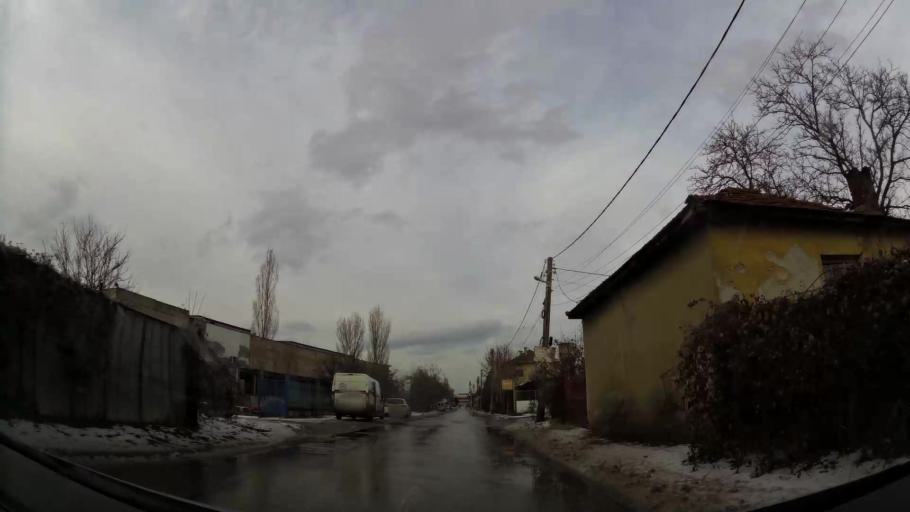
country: BG
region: Sofia-Capital
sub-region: Stolichna Obshtina
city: Sofia
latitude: 42.7233
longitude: 23.3297
